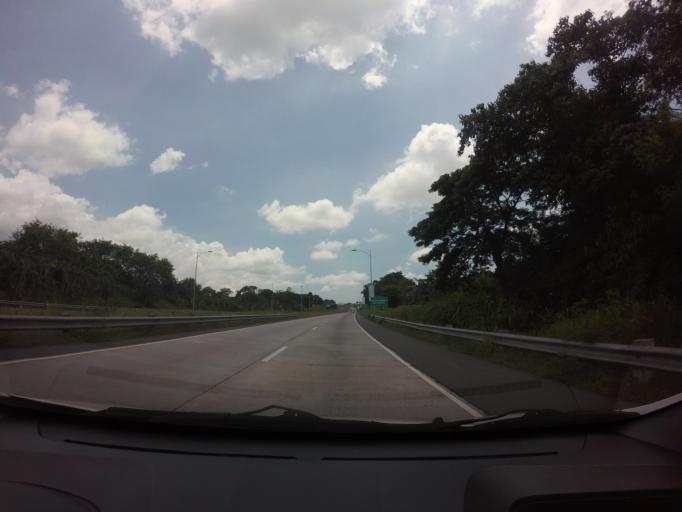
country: PH
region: Calabarzon
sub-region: Province of Laguna
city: San Pedro
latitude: 14.3771
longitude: 121.0277
